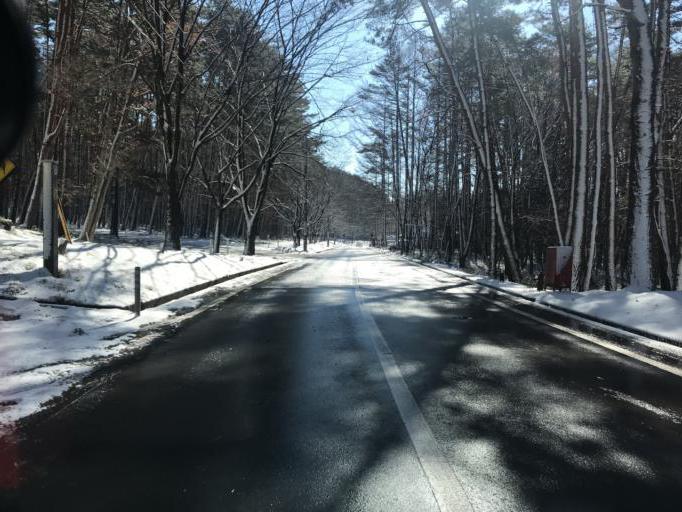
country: JP
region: Nagano
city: Chino
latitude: 35.8775
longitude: 138.3192
